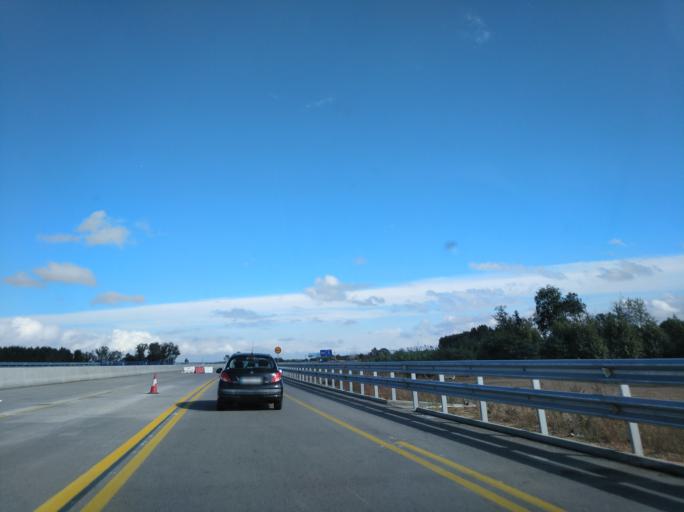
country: ES
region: Catalonia
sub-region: Provincia de Girona
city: Sils
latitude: 41.7889
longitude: 2.7571
